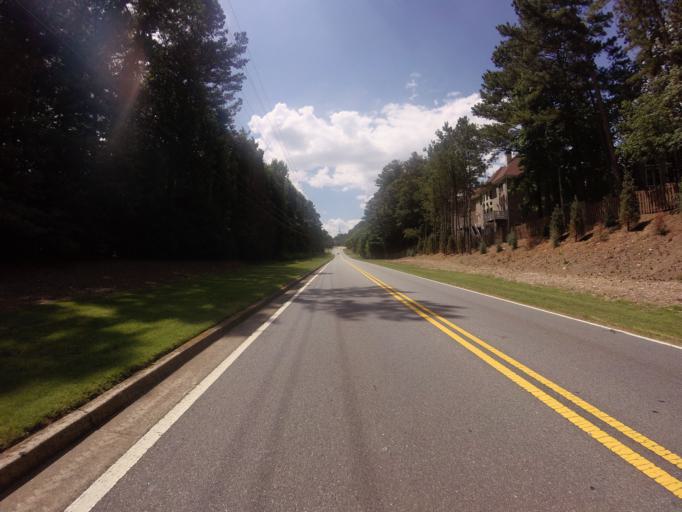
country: US
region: Georgia
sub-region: Fulton County
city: Johns Creek
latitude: 34.0210
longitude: -84.2468
